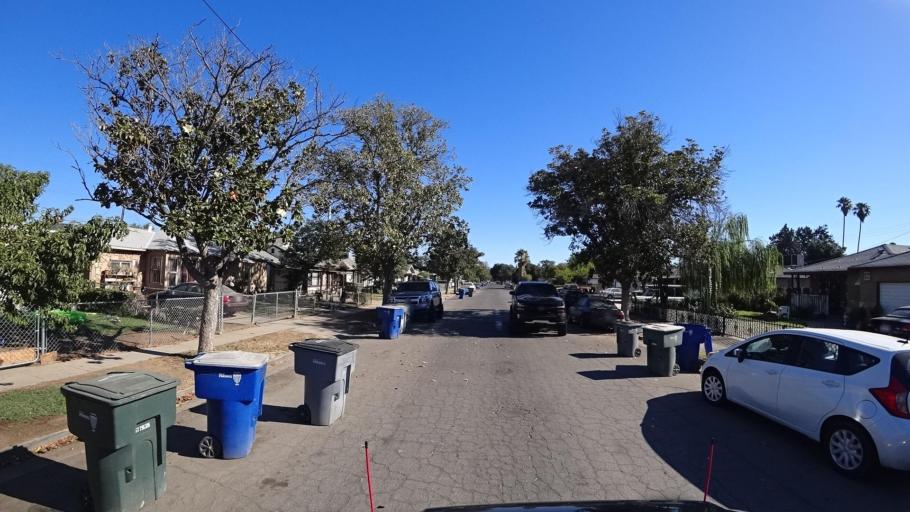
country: US
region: California
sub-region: Fresno County
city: Fresno
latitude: 36.7094
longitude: -119.7897
